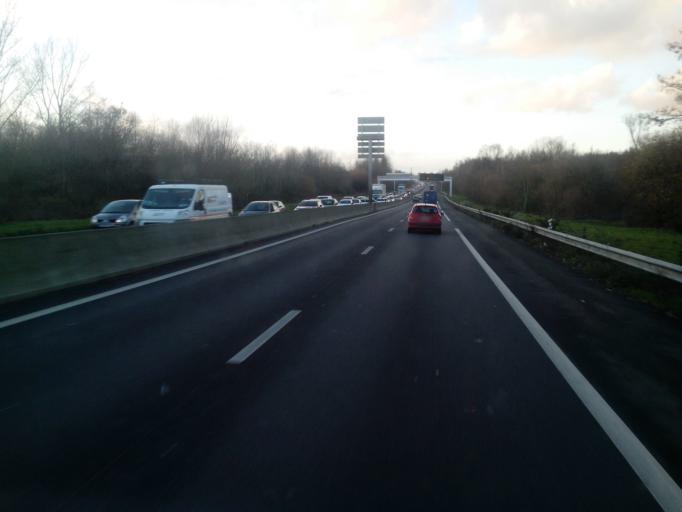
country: FR
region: Pays de la Loire
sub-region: Departement de la Loire-Atlantique
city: Sainte-Luce-sur-Loire
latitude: 47.2401
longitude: -1.4870
